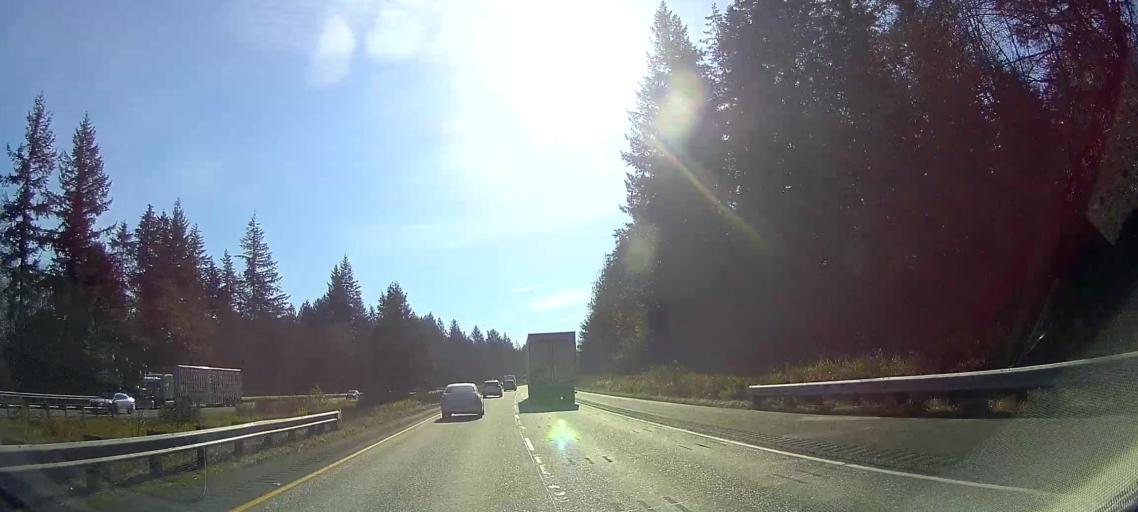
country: US
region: Washington
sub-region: Whatcom County
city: Sudden Valley
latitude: 48.6062
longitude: -122.3470
